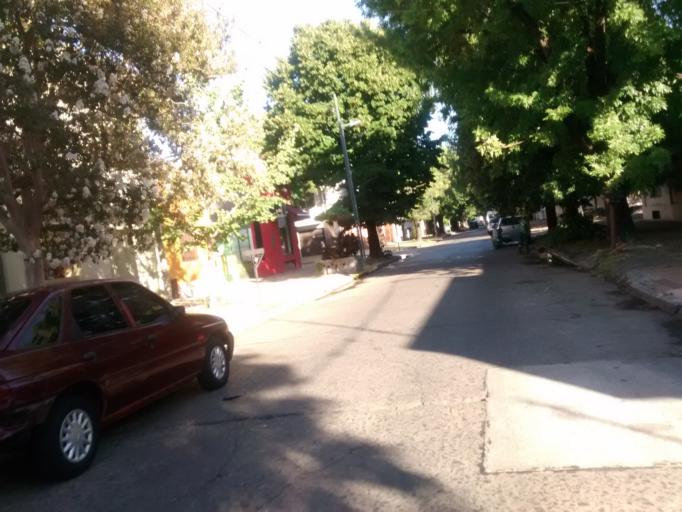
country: AR
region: Buenos Aires
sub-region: Partido de La Plata
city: La Plata
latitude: -34.9252
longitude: -57.9289
